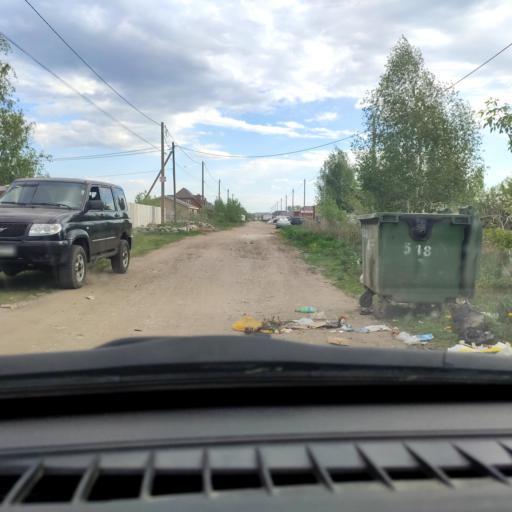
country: RU
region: Samara
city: Tol'yatti
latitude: 53.5720
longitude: 49.4113
